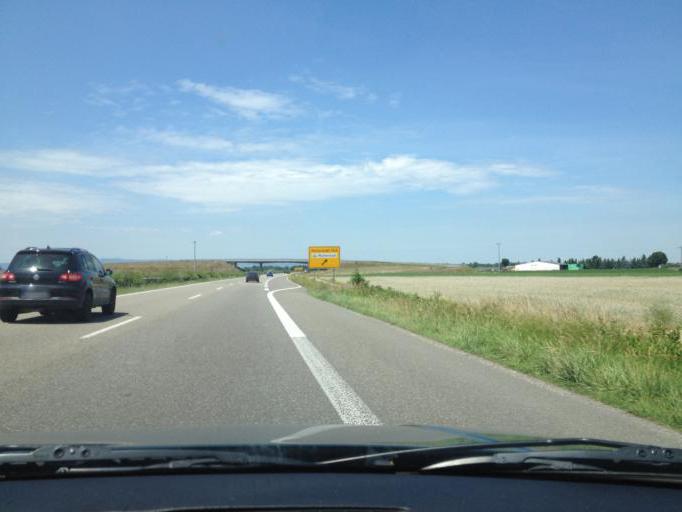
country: DE
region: Rheinland-Pfalz
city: Limburgerhof
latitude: 49.4362
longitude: 8.3890
